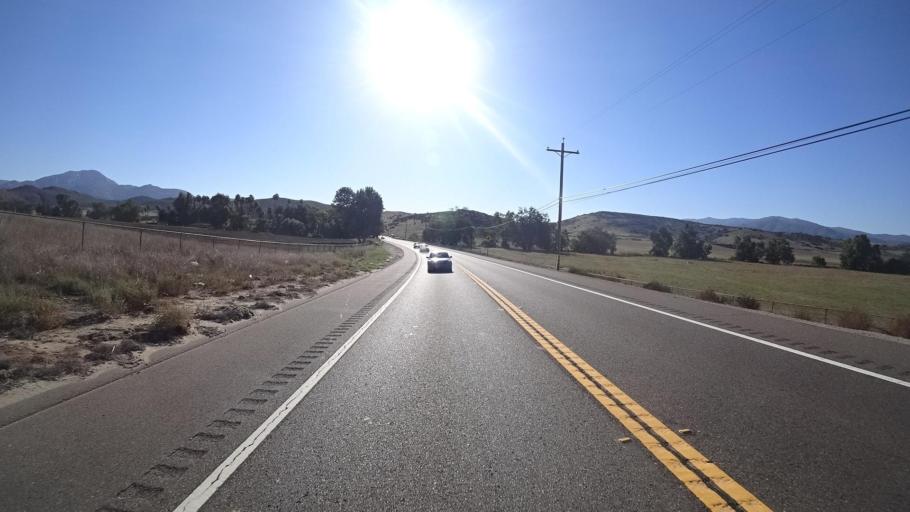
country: US
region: California
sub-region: San Diego County
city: Jamul
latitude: 32.6853
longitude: -116.8489
